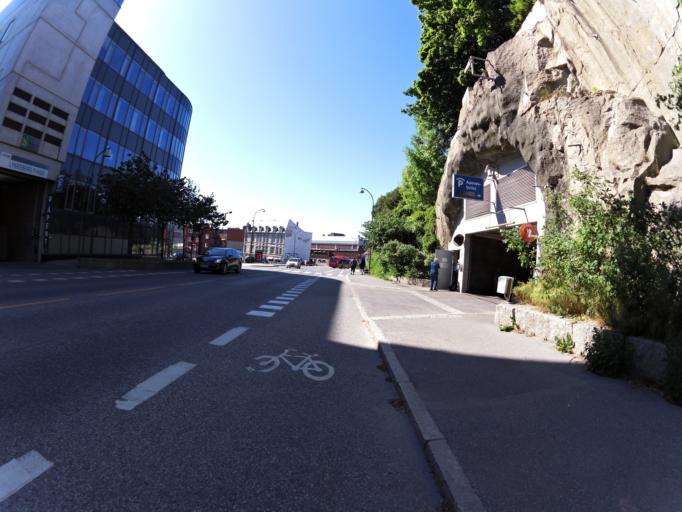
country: NO
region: Ostfold
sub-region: Fredrikstad
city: Fredrikstad
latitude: 59.2115
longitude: 10.9412
